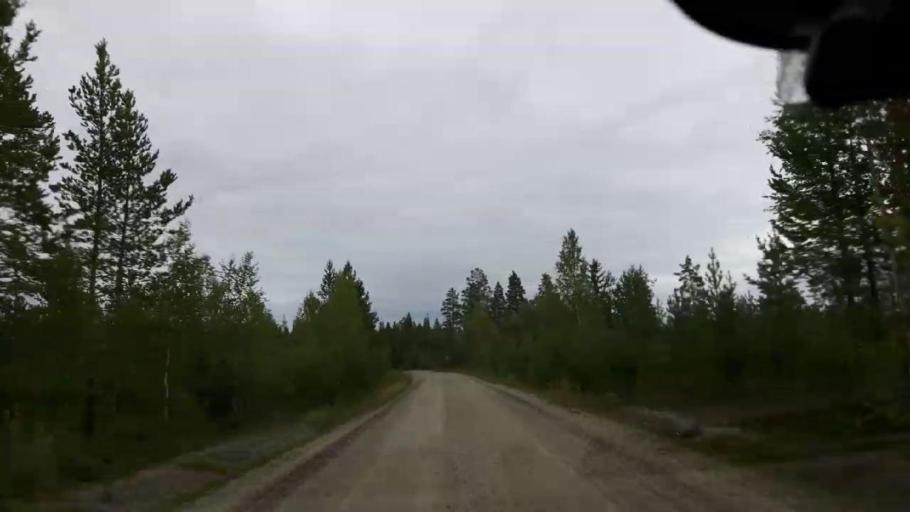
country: SE
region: Vaesternorrland
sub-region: Ange Kommun
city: Ange
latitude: 62.8122
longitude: 15.7235
